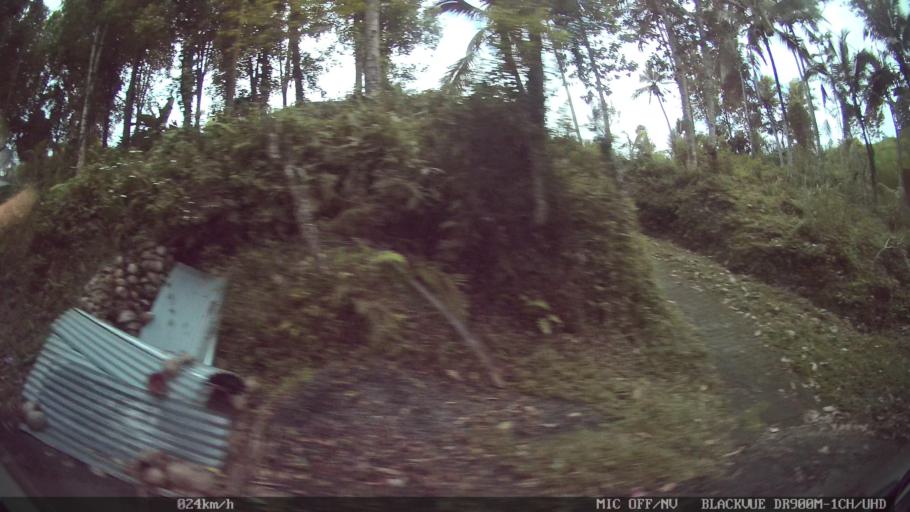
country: ID
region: Bali
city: Banjar Wangsian
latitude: -8.4601
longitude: 115.4159
